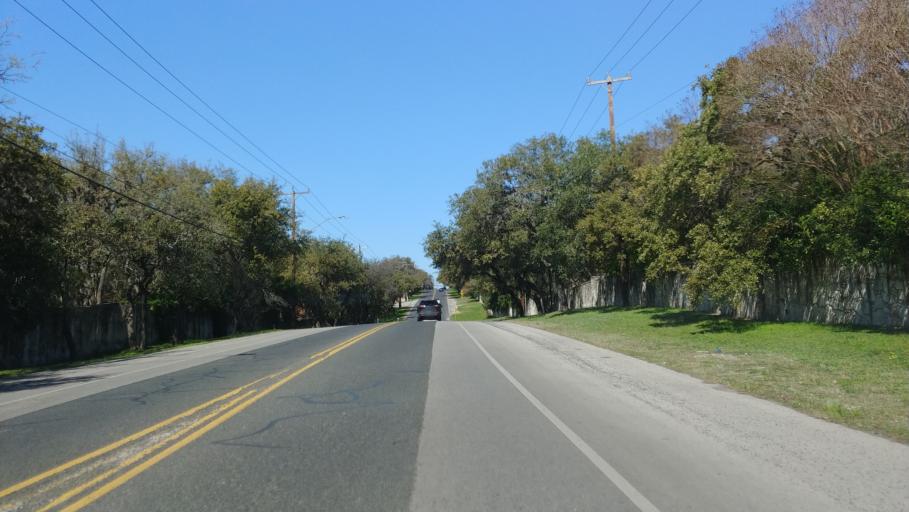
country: US
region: Texas
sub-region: Bexar County
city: Shavano Park
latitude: 29.5603
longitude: -98.5528
